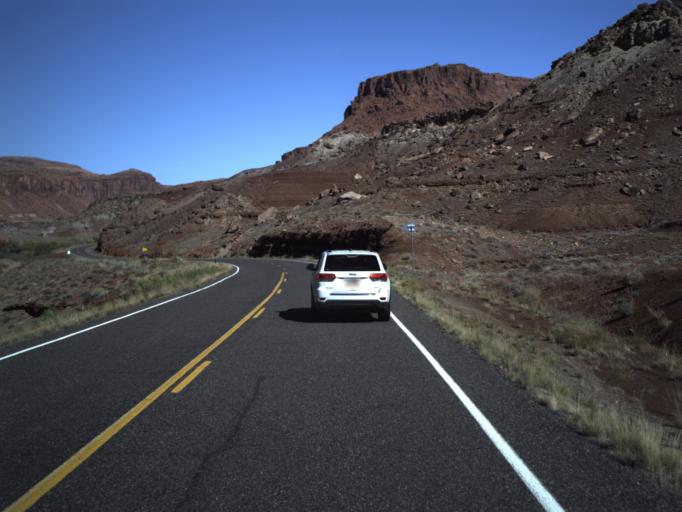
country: US
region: Utah
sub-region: San Juan County
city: Blanding
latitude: 37.8960
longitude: -110.4463
